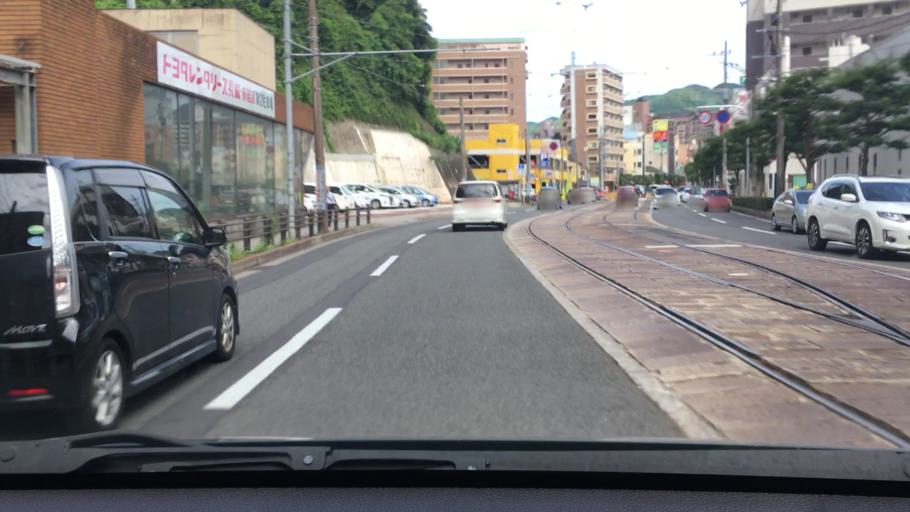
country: JP
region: Nagasaki
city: Obita
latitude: 32.7938
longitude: 129.8578
